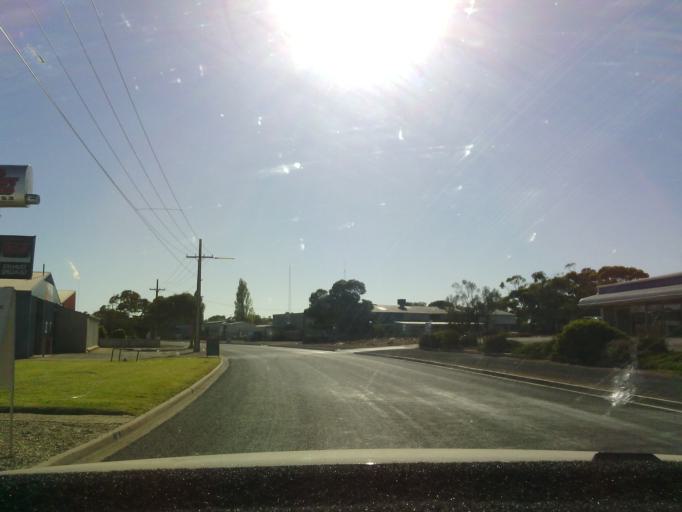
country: AU
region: South Australia
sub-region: Berri and Barmera
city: Berri
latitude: -34.2714
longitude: 140.6019
